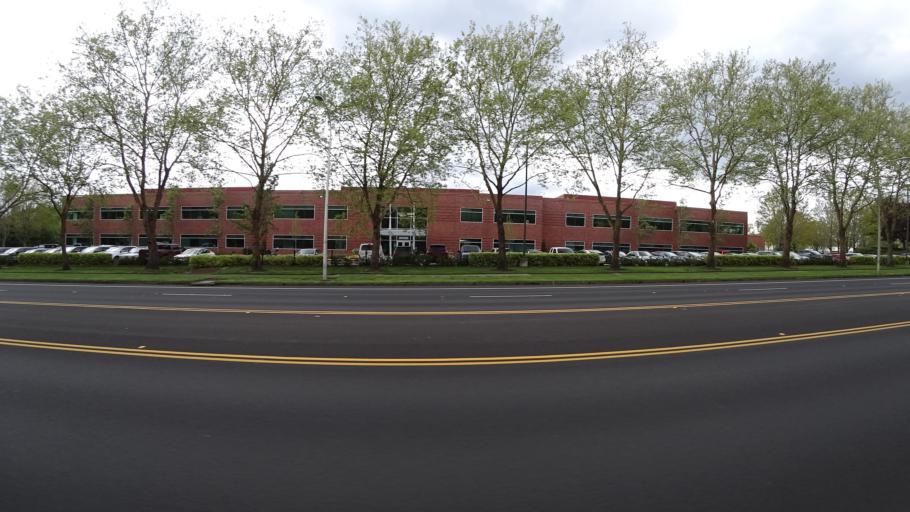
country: US
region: Oregon
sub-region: Washington County
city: Rockcreek
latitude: 45.5458
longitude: -122.8893
